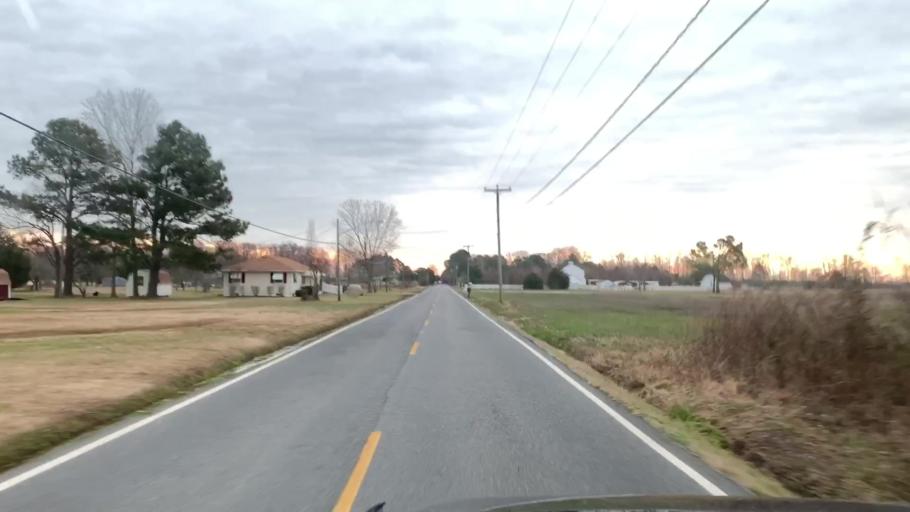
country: US
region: North Carolina
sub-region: Currituck County
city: Moyock
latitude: 36.6266
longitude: -76.1652
